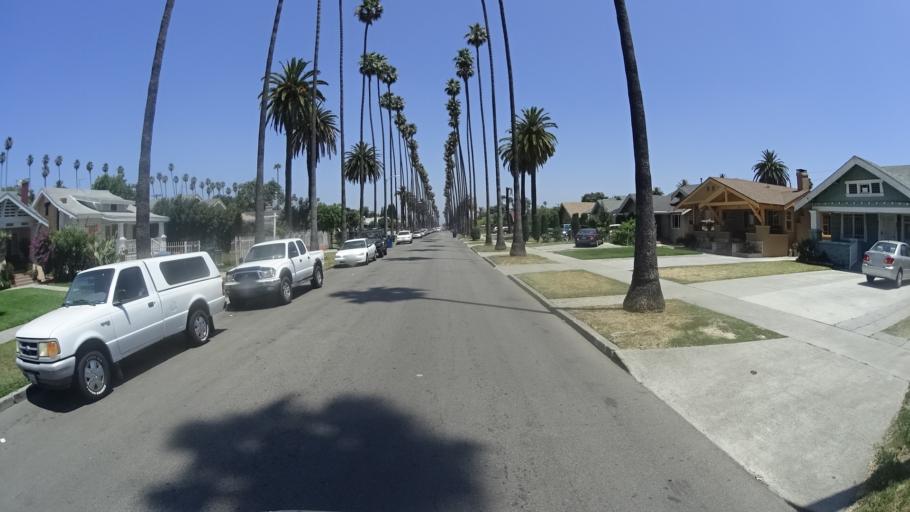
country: US
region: California
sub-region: Los Angeles County
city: View Park-Windsor Hills
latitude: 33.9969
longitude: -118.3160
